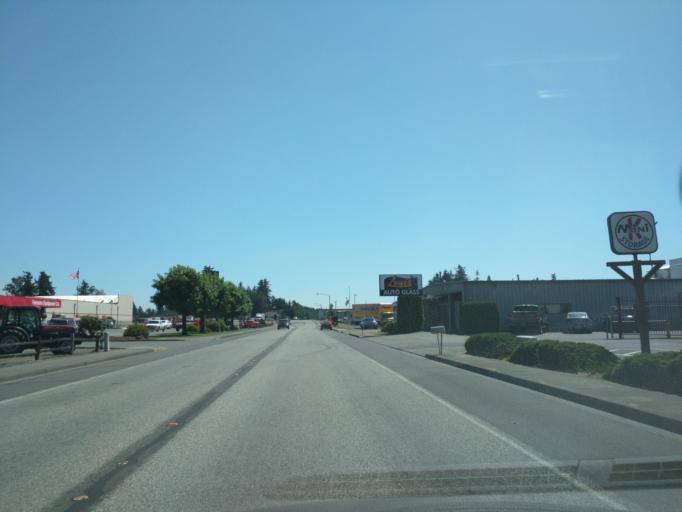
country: US
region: Washington
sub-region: Whatcom County
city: Lynden
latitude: 48.9422
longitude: -122.4810
